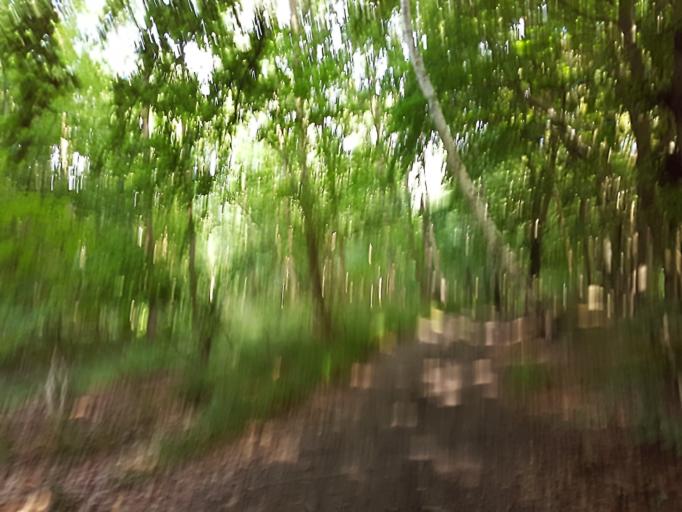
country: DK
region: Capital Region
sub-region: Egedal Kommune
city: Ganlose
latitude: 55.7971
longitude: 12.2919
